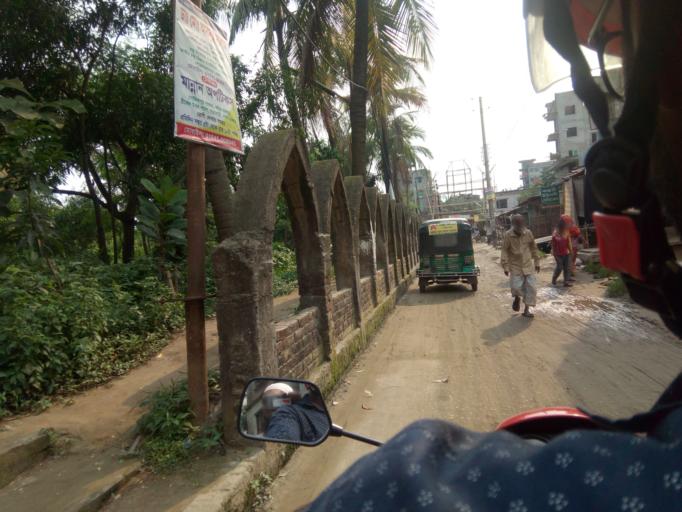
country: BD
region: Dhaka
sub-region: Dhaka
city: Dhaka
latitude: 23.7072
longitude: 90.4576
